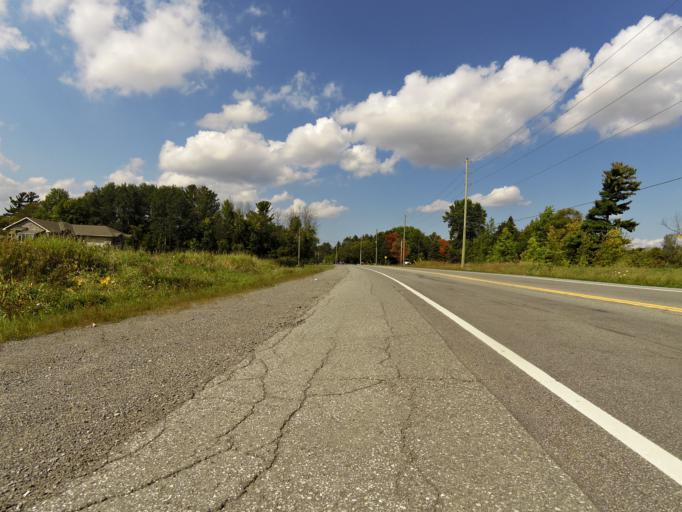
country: CA
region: Ontario
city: Bells Corners
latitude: 45.2412
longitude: -75.7036
